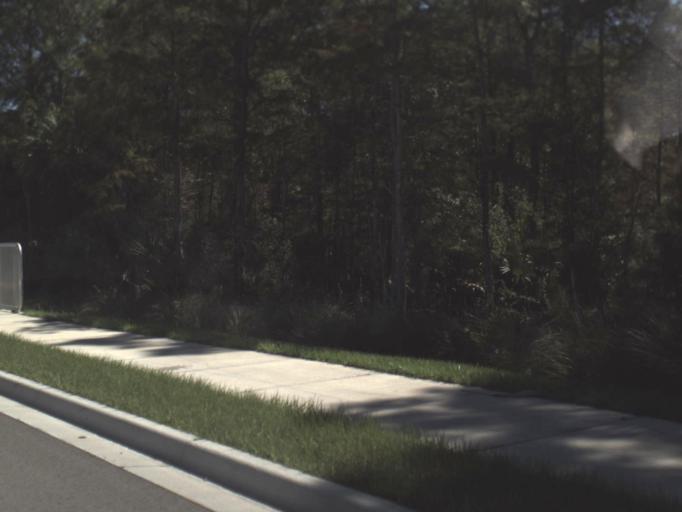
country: US
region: Florida
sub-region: Collier County
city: Golden Gate
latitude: 26.1540
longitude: -81.6962
